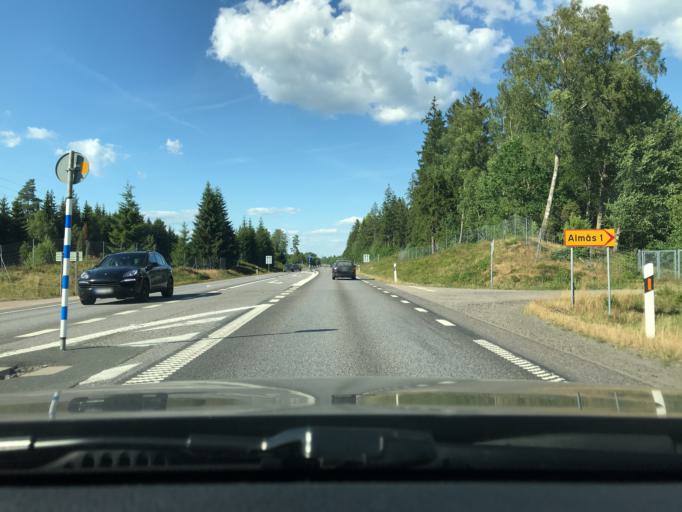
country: SE
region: Kronoberg
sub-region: Almhults Kommun
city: AElmhult
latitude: 56.5110
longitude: 14.1305
